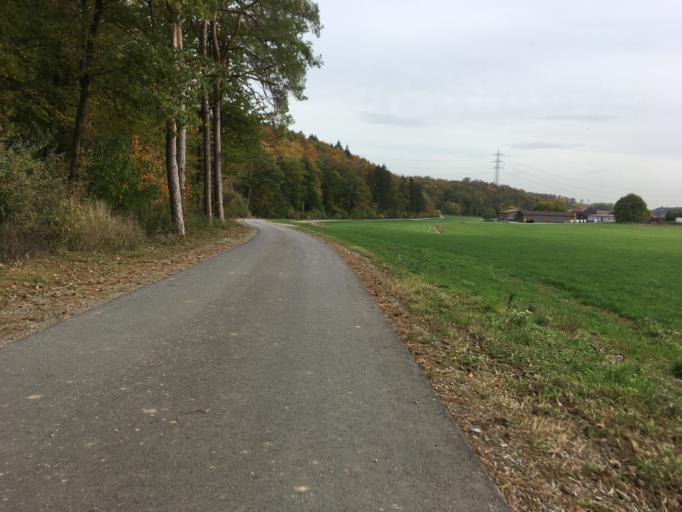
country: DE
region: Baden-Wuerttemberg
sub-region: Karlsruhe Region
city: Buchen
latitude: 49.4929
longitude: 9.3391
